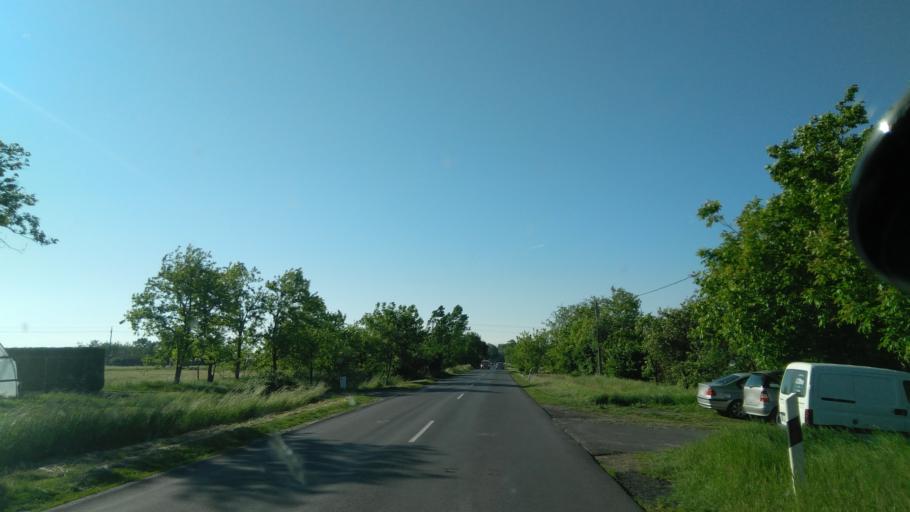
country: HU
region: Bekes
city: Gyula
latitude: 46.6292
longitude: 21.2586
